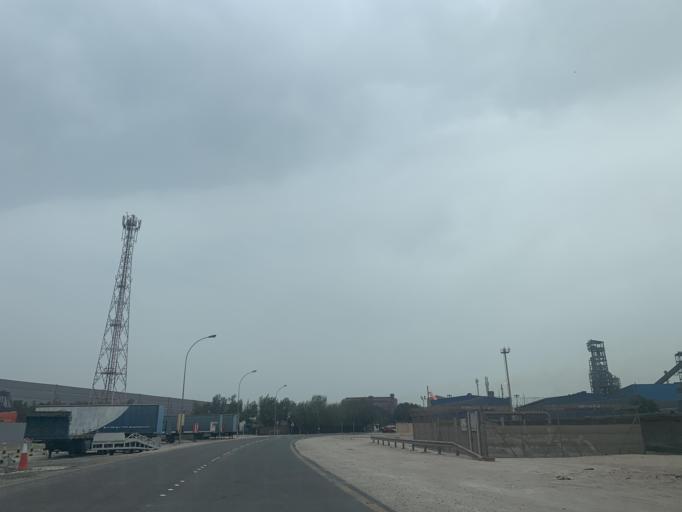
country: BH
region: Muharraq
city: Al Hadd
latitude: 26.2044
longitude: 50.6776
